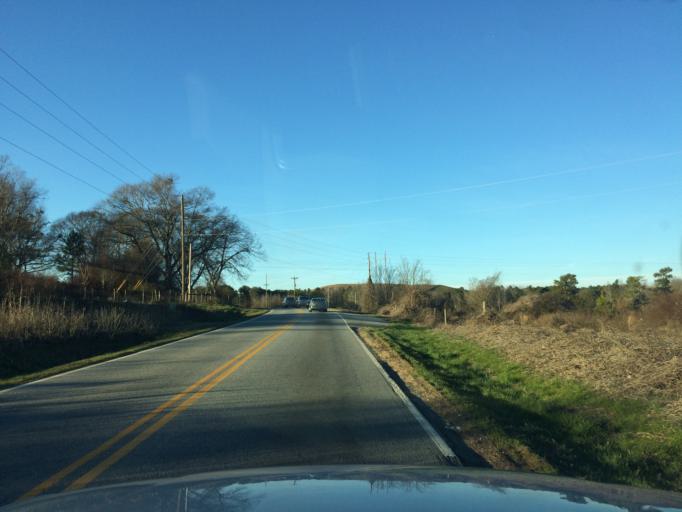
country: US
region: Georgia
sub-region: Barrow County
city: Winder
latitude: 33.9549
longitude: -83.7687
